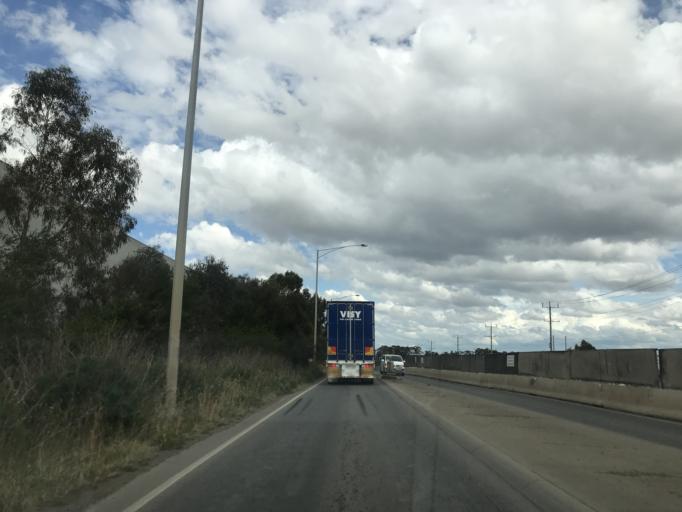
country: AU
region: Victoria
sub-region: Wyndham
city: Truganina
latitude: -37.8067
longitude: 144.7515
